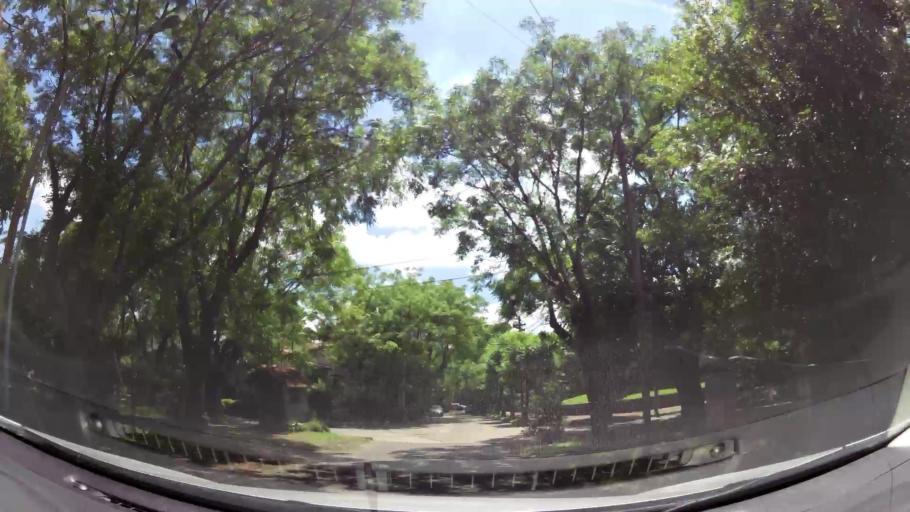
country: AR
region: Buenos Aires
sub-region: Partido de Tigre
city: Tigre
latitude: -34.4204
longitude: -58.5863
